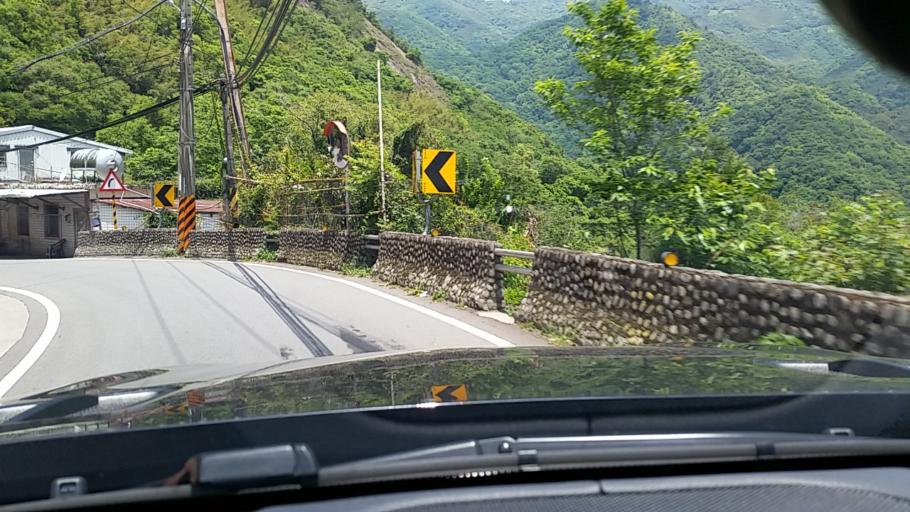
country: TW
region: Taiwan
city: Daxi
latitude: 24.6938
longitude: 121.3744
